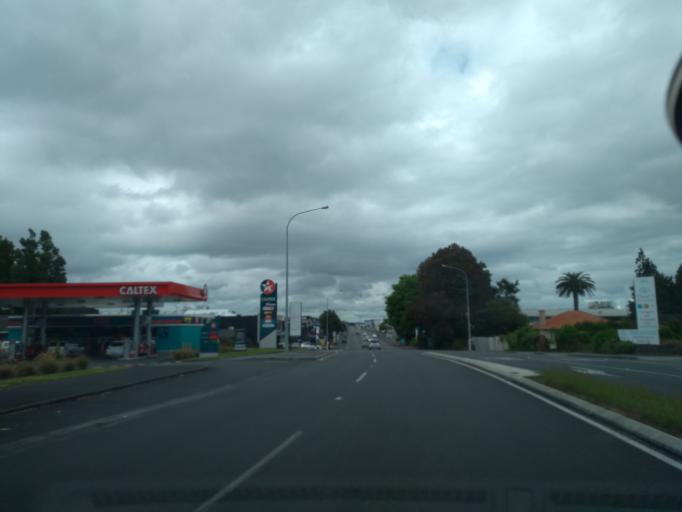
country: NZ
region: Auckland
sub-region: Auckland
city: Tamaki
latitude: -36.9034
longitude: 174.8081
